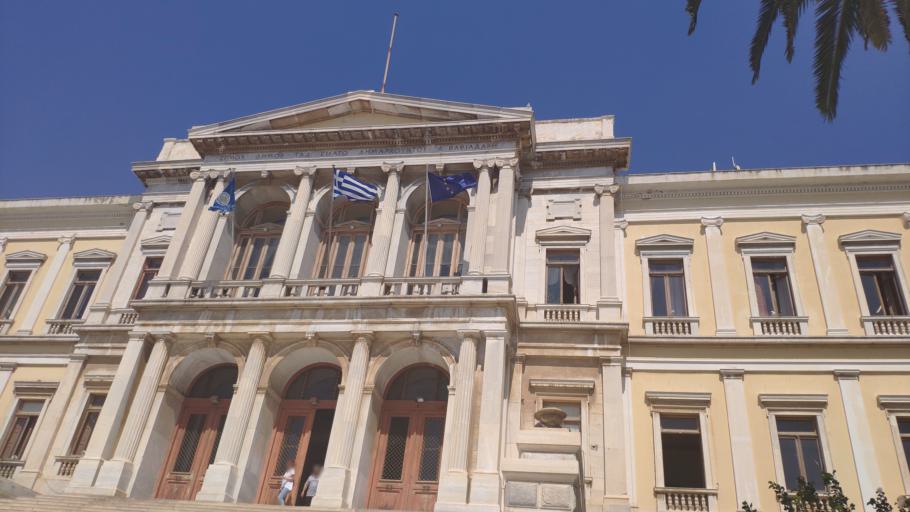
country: GR
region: South Aegean
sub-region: Nomos Kykladon
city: Ermoupolis
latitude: 37.4447
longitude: 24.9430
